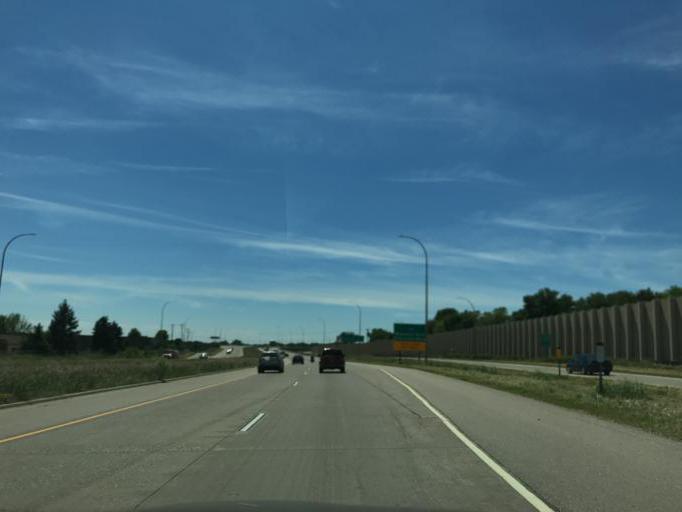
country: US
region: Minnesota
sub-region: Hennepin County
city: Osseo
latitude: 45.1154
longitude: -93.3911
